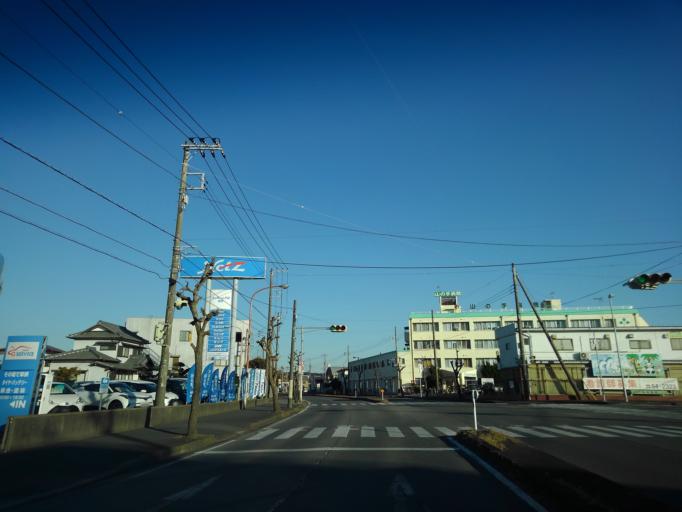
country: JP
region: Chiba
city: Kimitsu
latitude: 35.3178
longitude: 139.9216
